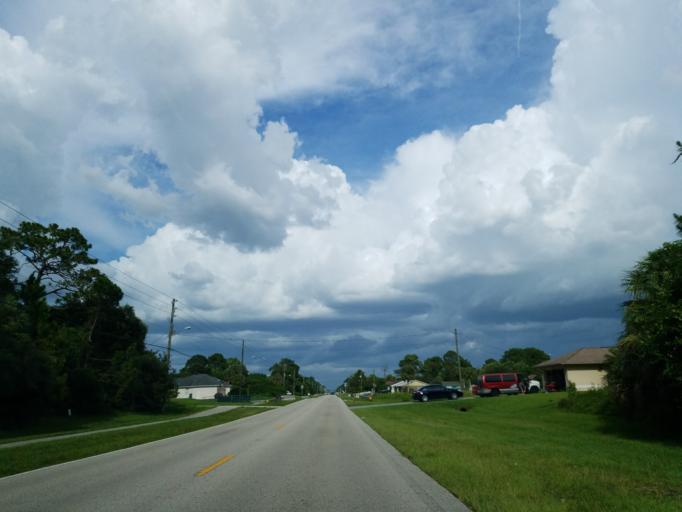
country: US
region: Florida
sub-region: Sarasota County
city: North Port
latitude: 27.0689
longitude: -82.1932
